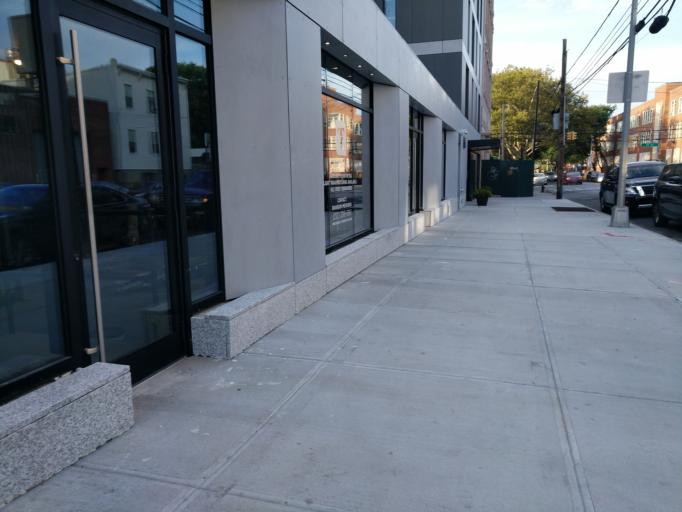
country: US
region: New York
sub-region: Queens County
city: Long Island City
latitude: 40.7565
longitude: -73.9352
